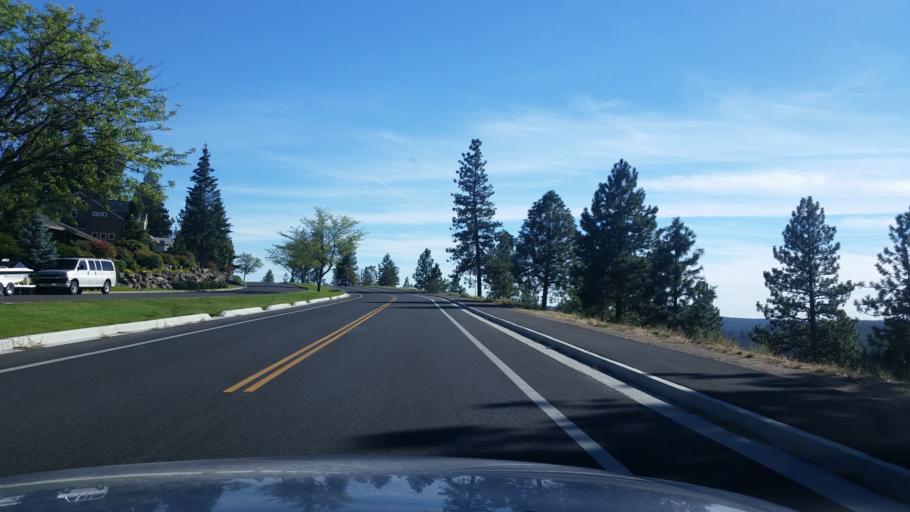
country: US
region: Washington
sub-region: Spokane County
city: Spokane
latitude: 47.6257
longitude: -117.4291
